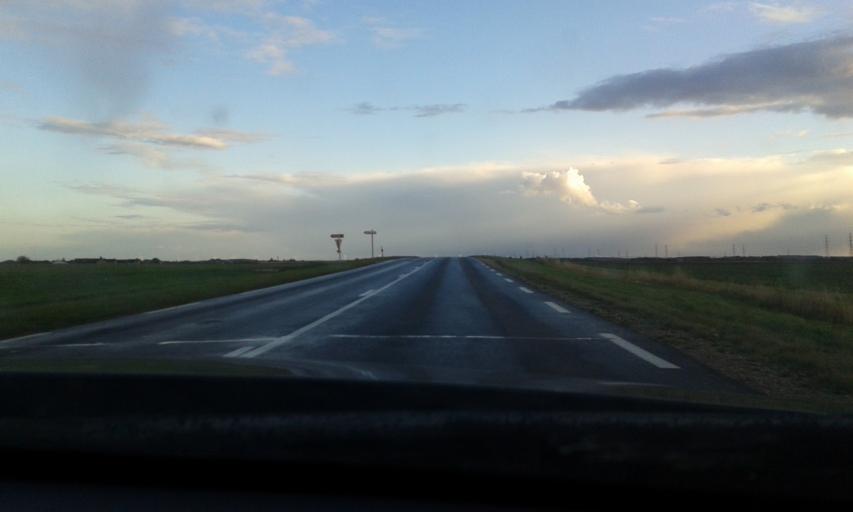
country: FR
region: Centre
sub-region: Departement d'Eure-et-Loir
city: Janville
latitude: 48.2455
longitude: 1.7744
